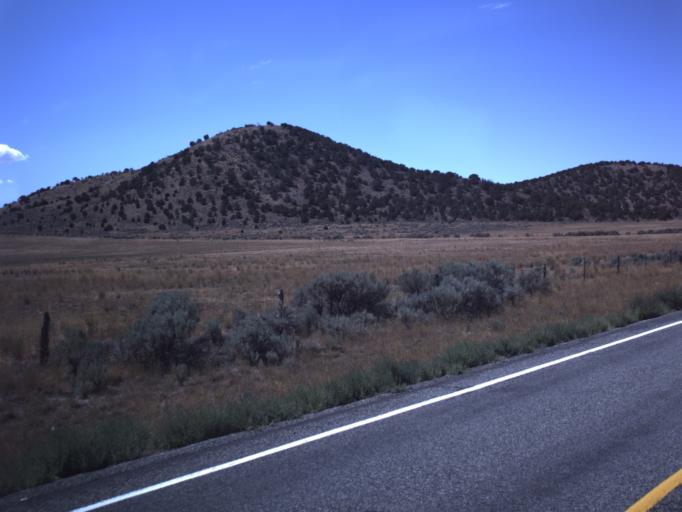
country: US
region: Utah
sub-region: Juab County
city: Nephi
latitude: 39.6973
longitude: -111.9713
